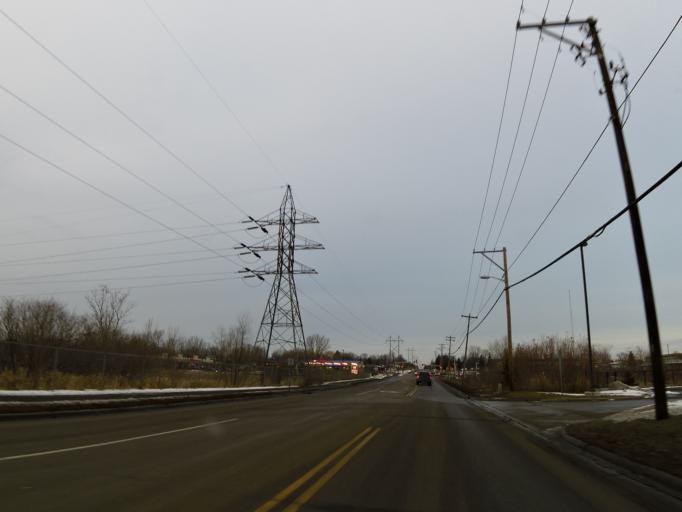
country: US
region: Minnesota
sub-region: Washington County
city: Oakdale
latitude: 44.9950
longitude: -92.9645
